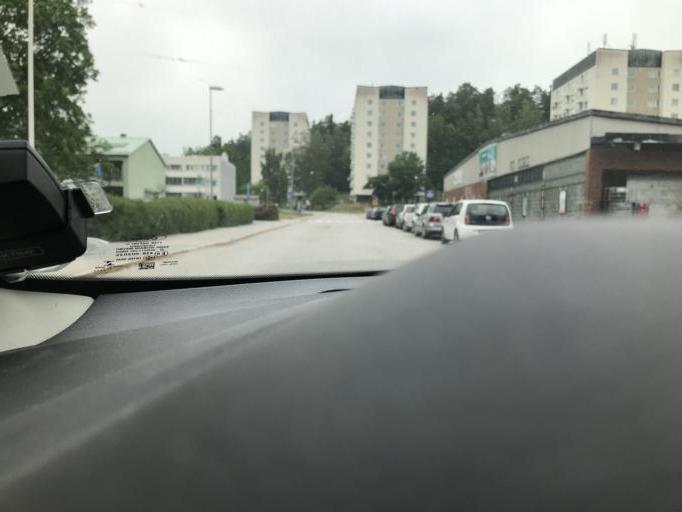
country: SE
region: Stockholm
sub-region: Botkyrka Kommun
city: Tumba
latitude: 59.2057
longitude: 17.8270
